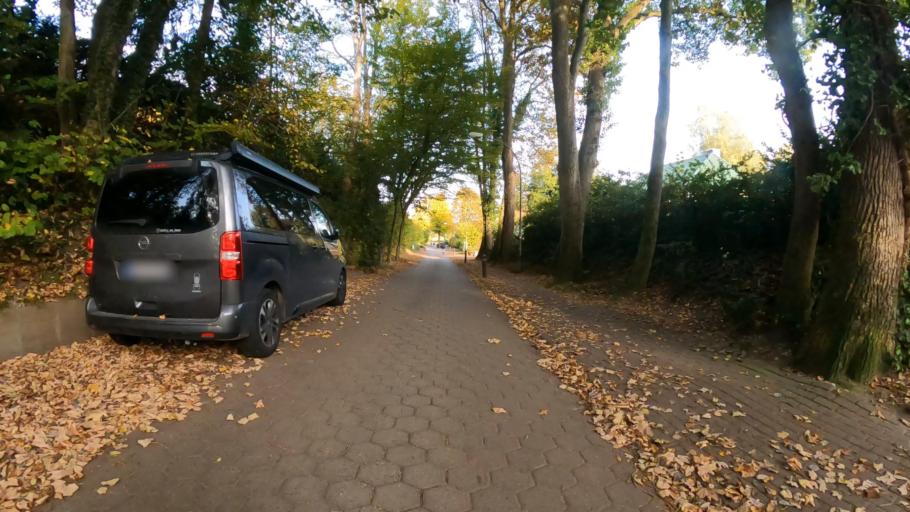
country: DE
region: Lower Saxony
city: Bendestorf
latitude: 53.3428
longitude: 9.9731
